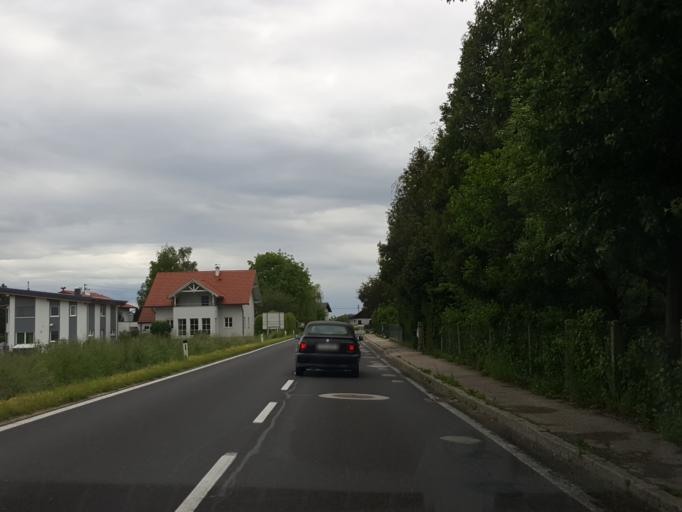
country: AT
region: Upper Austria
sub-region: Politischer Bezirk Vocklabruck
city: Seewalchen
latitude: 47.9600
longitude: 13.5745
